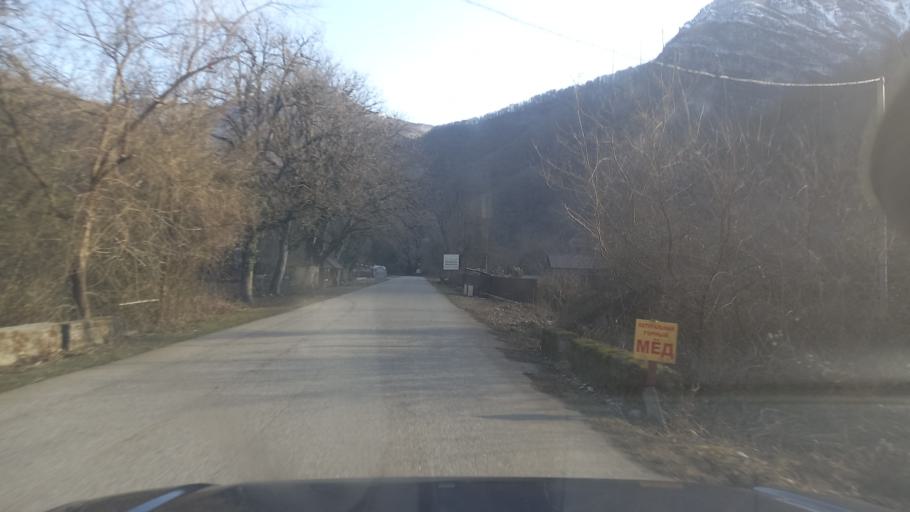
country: GE
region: Abkhazia
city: Gagra
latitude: 43.3037
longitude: 40.4023
